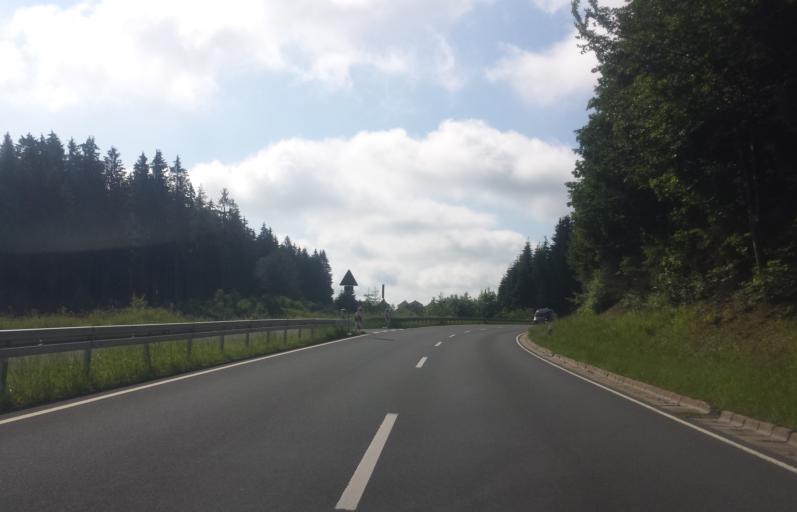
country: DE
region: Bavaria
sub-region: Upper Franconia
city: Ludwigsstadt
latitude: 50.4483
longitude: 11.3732
